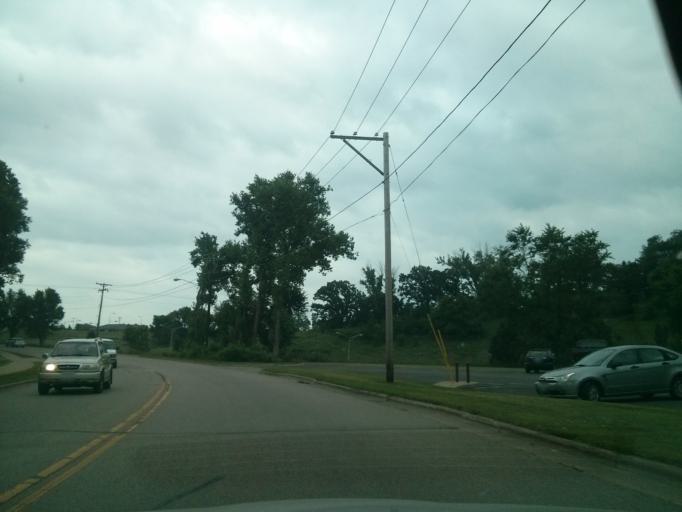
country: US
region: Wisconsin
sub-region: Saint Croix County
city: Hudson
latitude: 44.9635
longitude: -92.7476
